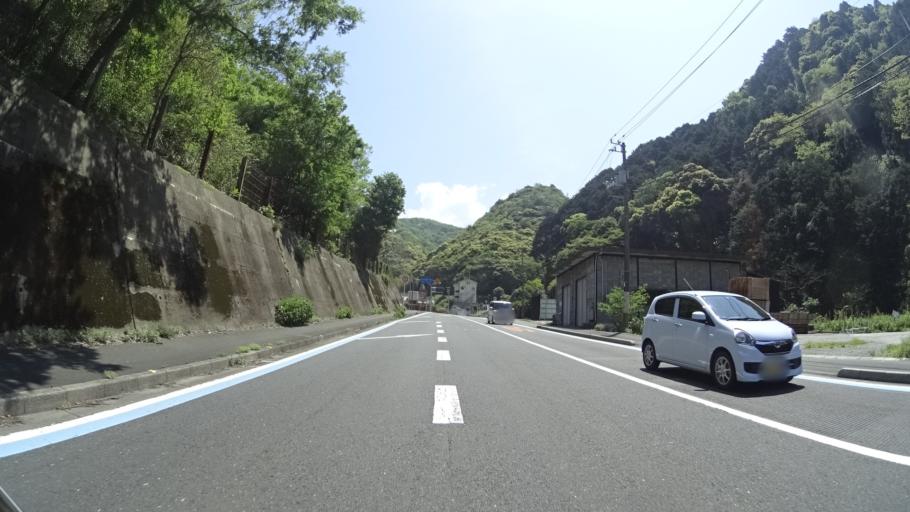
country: JP
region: Ehime
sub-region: Nishiuwa-gun
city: Ikata-cho
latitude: 33.4976
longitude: 132.3752
